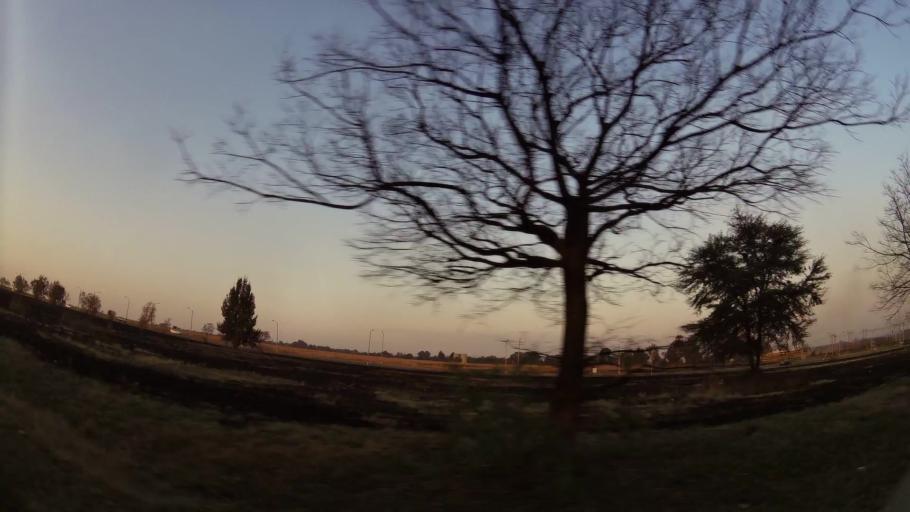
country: ZA
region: Gauteng
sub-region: Ekurhuleni Metropolitan Municipality
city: Springs
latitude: -26.3148
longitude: 28.4543
